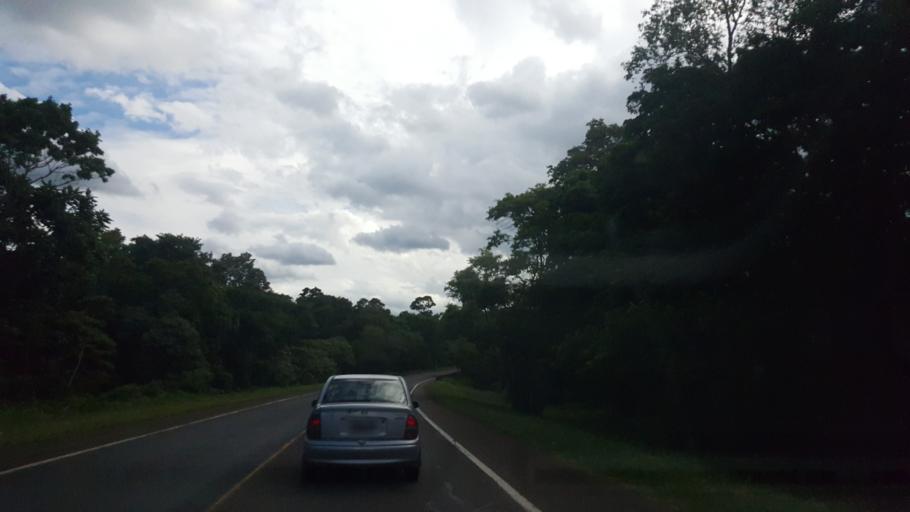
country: AR
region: Misiones
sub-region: Departamento de Iguazu
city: Puerto Iguazu
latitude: -25.7165
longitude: -54.5200
